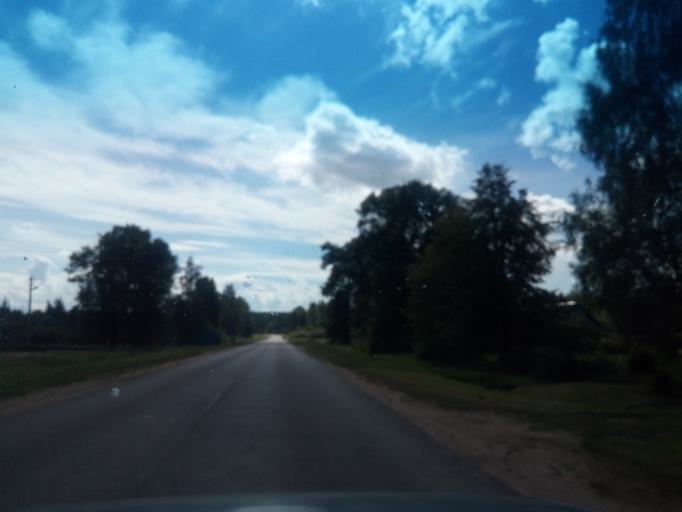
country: BY
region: Vitebsk
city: Dzisna
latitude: 55.6576
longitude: 28.3232
